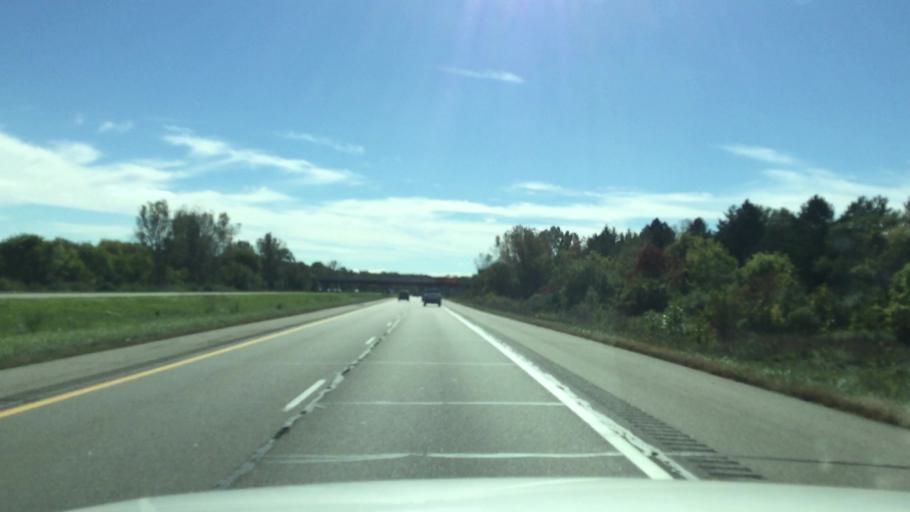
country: US
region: Michigan
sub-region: Washtenaw County
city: Ypsilanti
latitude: 42.3522
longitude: -83.5915
